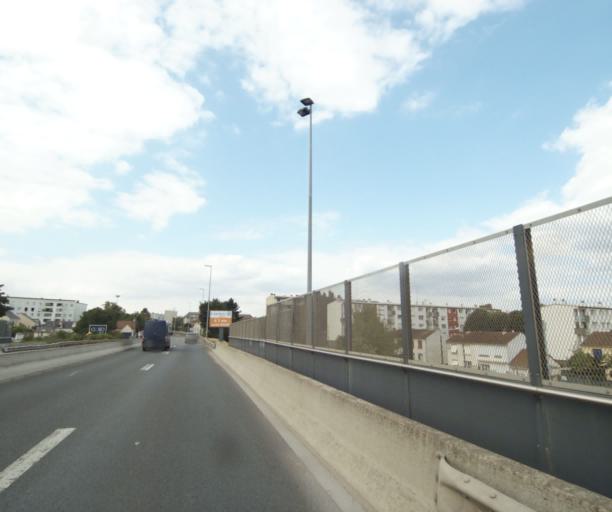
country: FR
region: Centre
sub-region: Departement du Loiret
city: Saint-Jean-de-la-Ruelle
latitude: 47.9026
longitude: 1.8721
